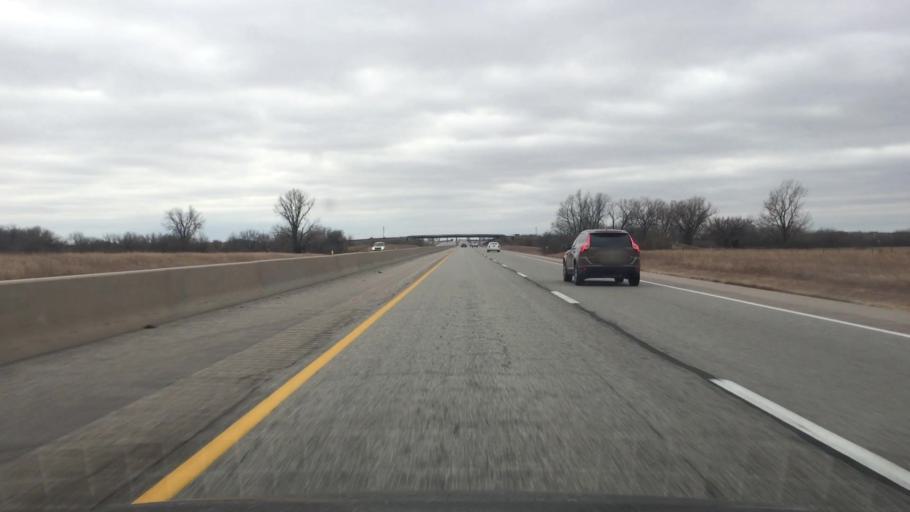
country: US
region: Kansas
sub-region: Butler County
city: El Dorado
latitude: 38.0324
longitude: -96.6560
